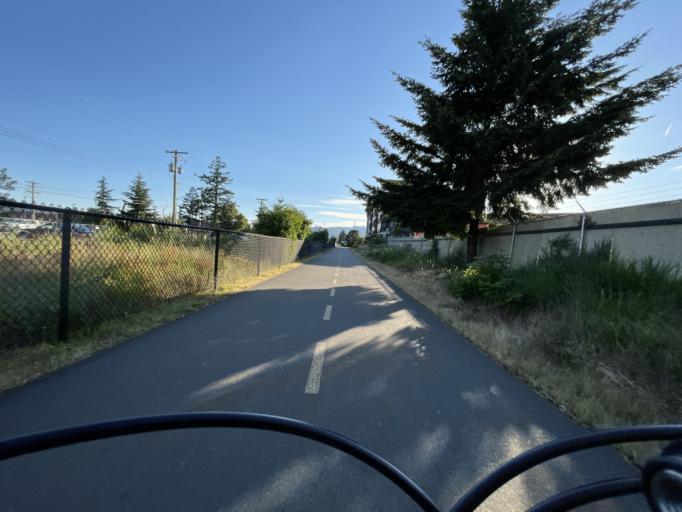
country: CA
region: British Columbia
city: Langford
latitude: 48.4453
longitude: -123.5069
